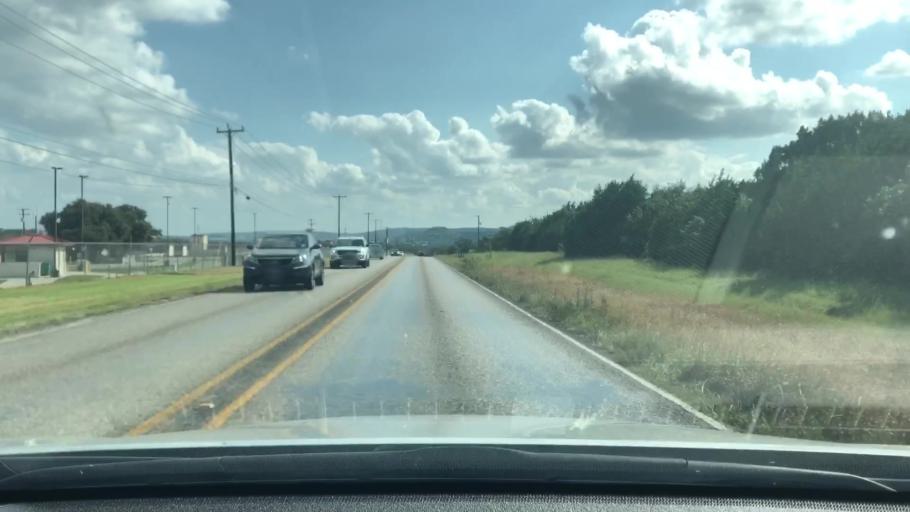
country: US
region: Texas
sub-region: Bexar County
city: Cross Mountain
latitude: 29.6864
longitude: -98.6316
